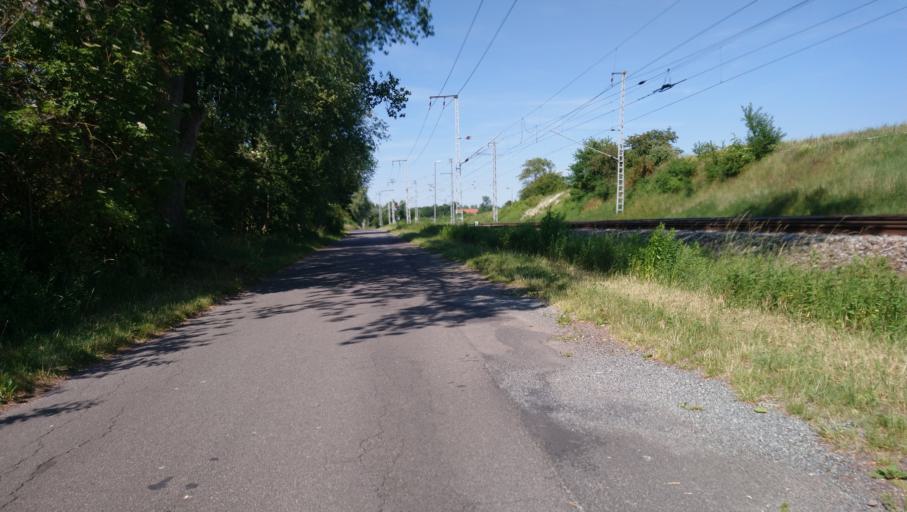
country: DE
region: Mecklenburg-Vorpommern
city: Dierkow-Neu
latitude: 54.0885
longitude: 12.1781
